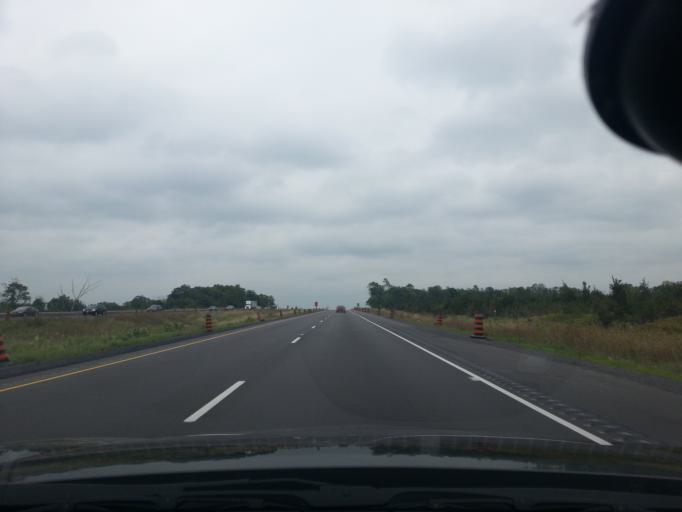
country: CA
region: Ontario
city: Skatepark
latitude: 44.2760
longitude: -76.8598
